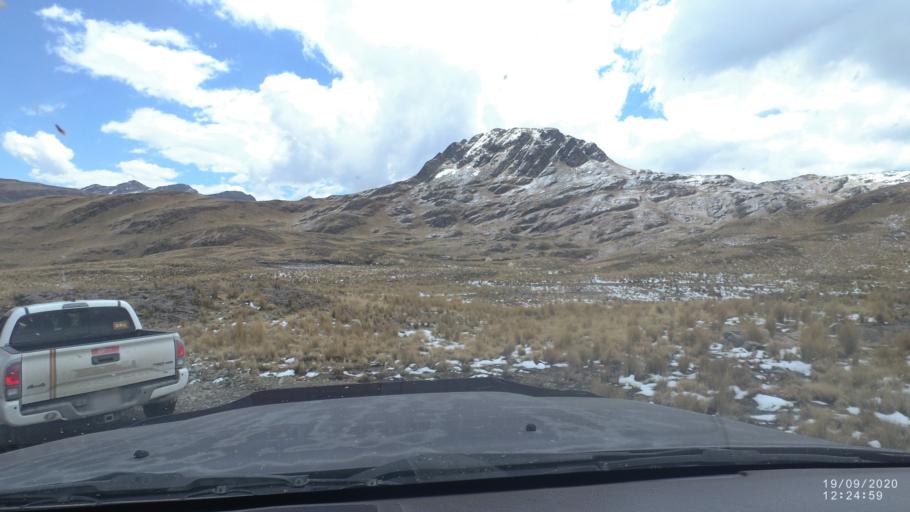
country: BO
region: Cochabamba
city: Cochabamba
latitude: -17.2935
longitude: -66.1101
